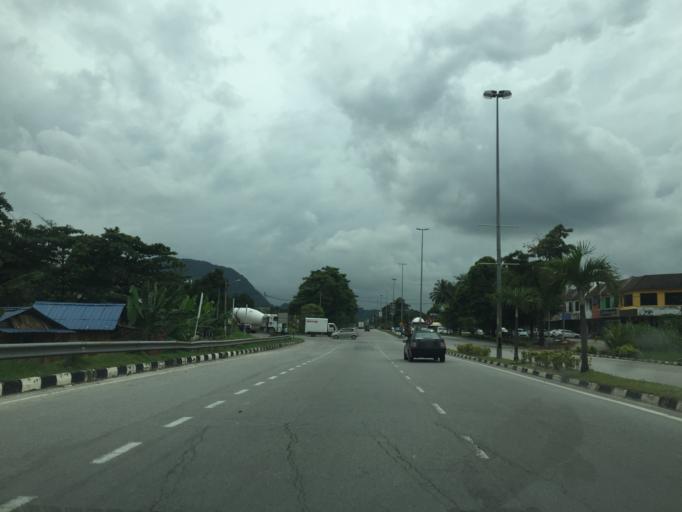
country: MY
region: Perak
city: Ipoh
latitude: 4.5411
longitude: 101.1226
